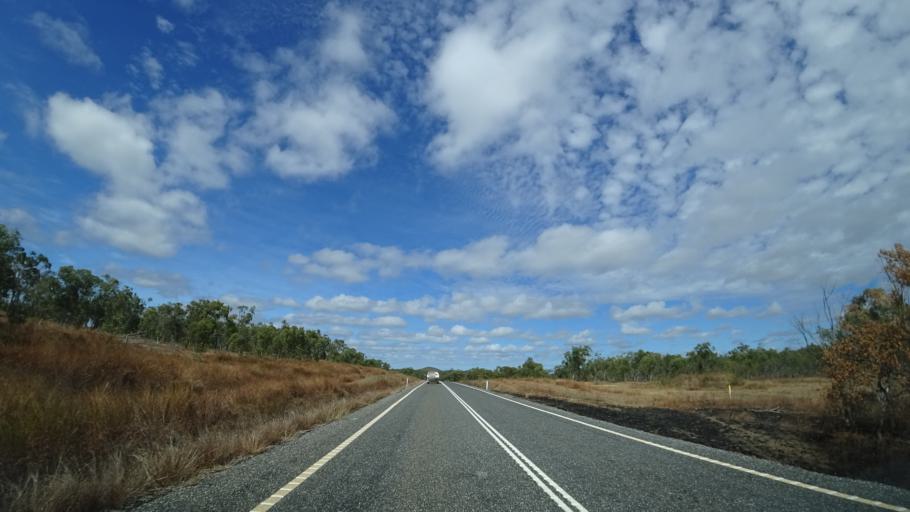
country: AU
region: Queensland
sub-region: Cairns
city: Port Douglas
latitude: -16.3822
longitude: 144.7364
